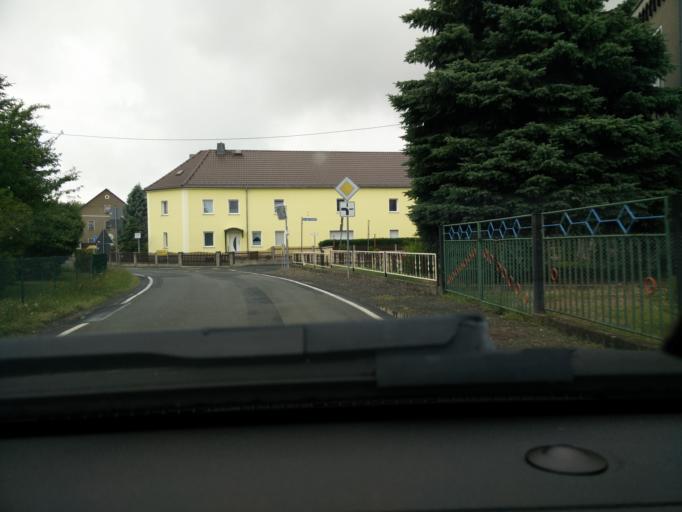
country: DE
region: Saxony
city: Grossbardau
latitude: 51.1801
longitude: 12.6930
